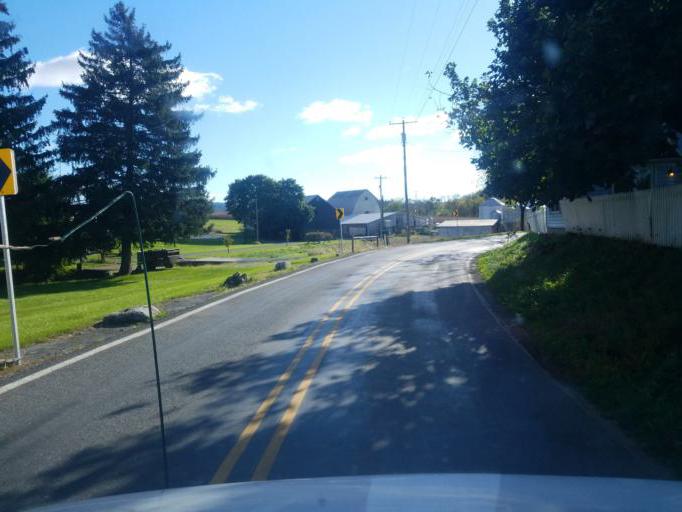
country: US
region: Pennsylvania
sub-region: Franklin County
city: Guilford Siding
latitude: 39.8081
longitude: -77.6141
